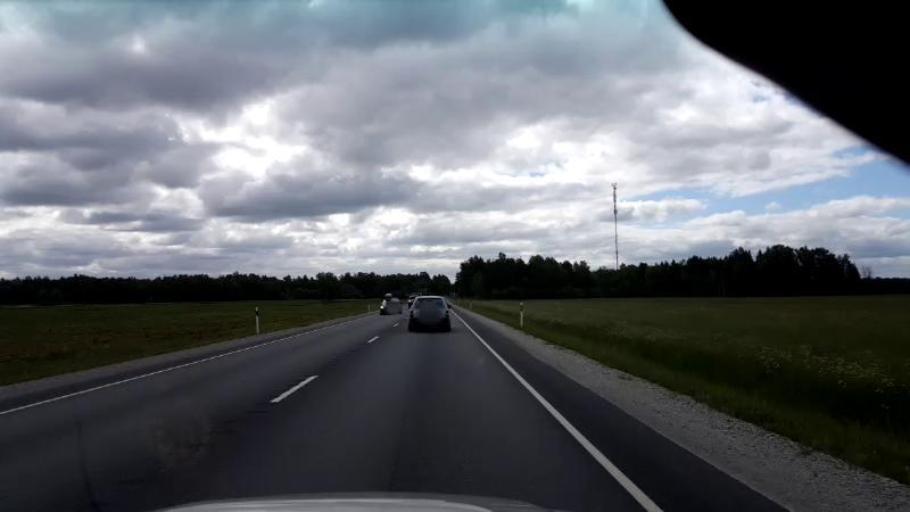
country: EE
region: Paernumaa
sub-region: Halinga vald
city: Parnu-Jaagupi
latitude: 58.6599
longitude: 24.4691
